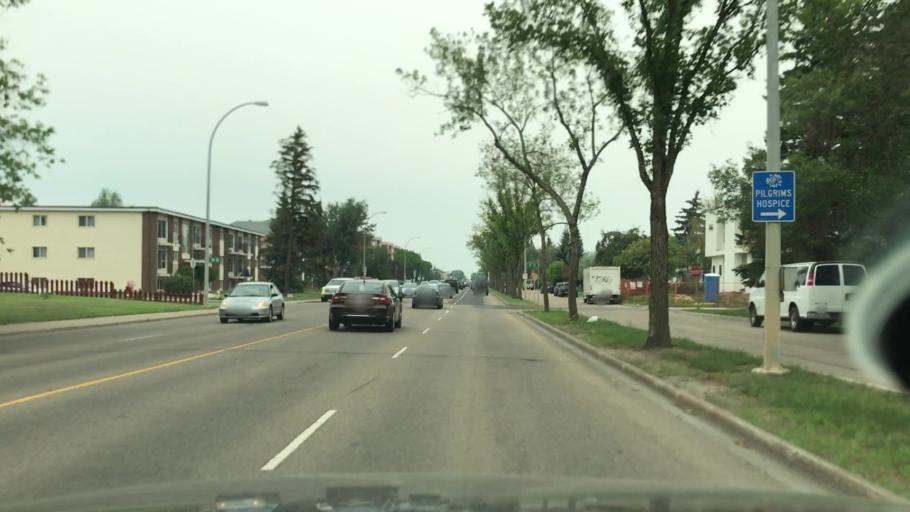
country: CA
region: Alberta
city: Edmonton
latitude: 53.5356
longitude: -113.5779
